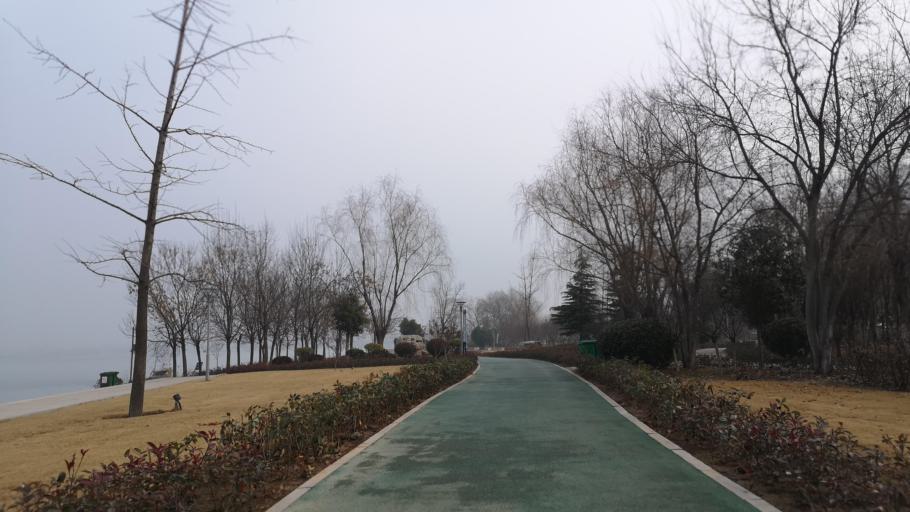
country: CN
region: Henan Sheng
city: Zhongyuanlu
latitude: 35.8005
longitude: 115.0498
